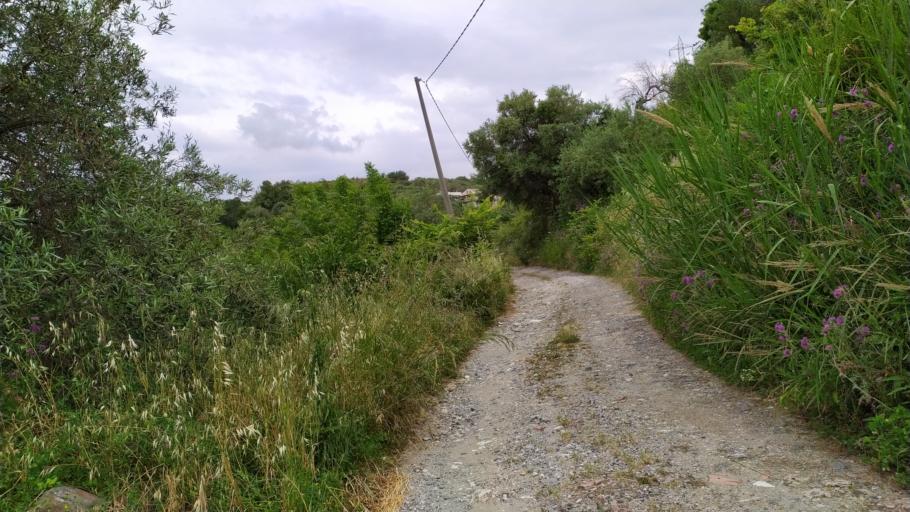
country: IT
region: Sicily
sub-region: Messina
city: Gualtieri Sicamino
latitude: 38.1560
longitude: 15.2993
